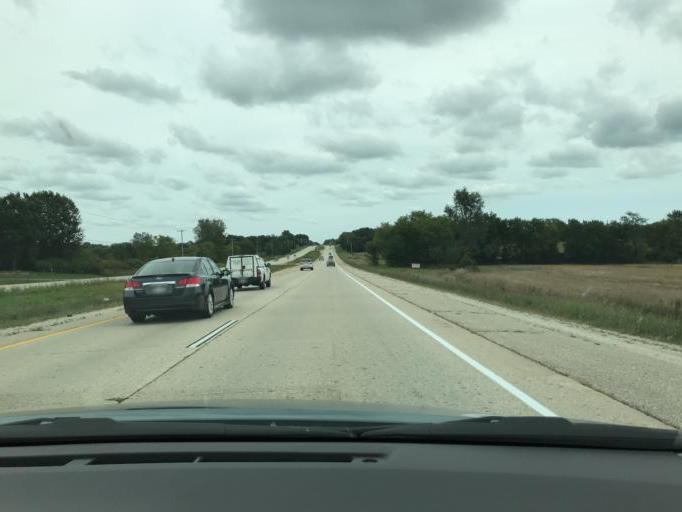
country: US
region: Wisconsin
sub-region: Kenosha County
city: Paddock Lake
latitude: 42.5680
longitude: -88.0872
